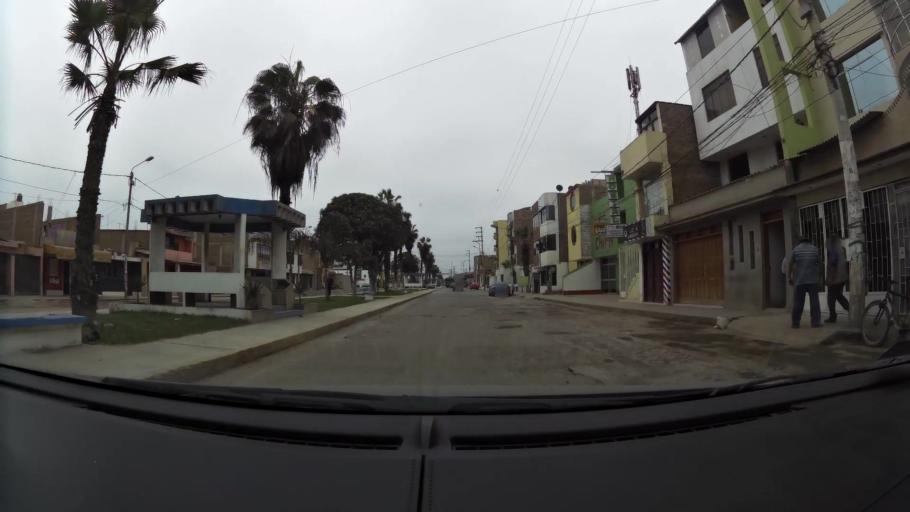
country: PE
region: La Libertad
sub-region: Provincia de Trujillo
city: Buenos Aires
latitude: -8.1422
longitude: -79.0539
